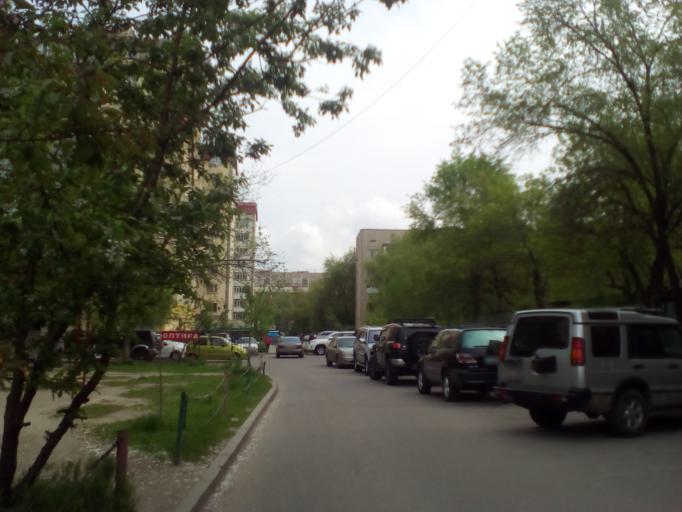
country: KZ
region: Almaty Qalasy
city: Almaty
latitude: 43.2369
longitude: 76.8251
